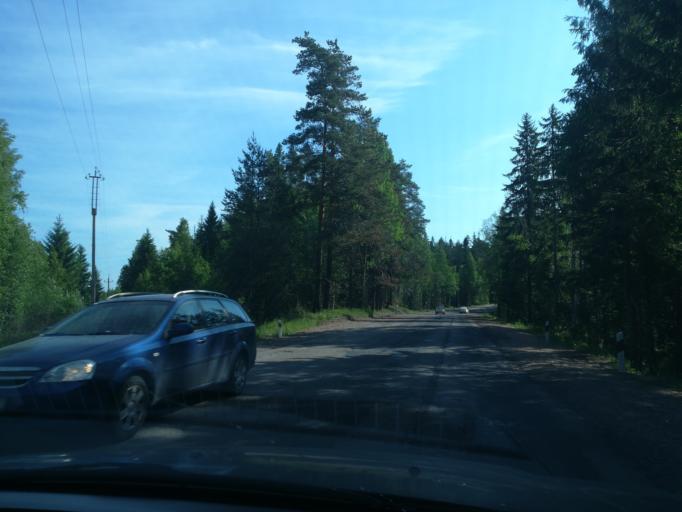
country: RU
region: Leningrad
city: Lesogorskiy
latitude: 60.9007
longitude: 28.8468
